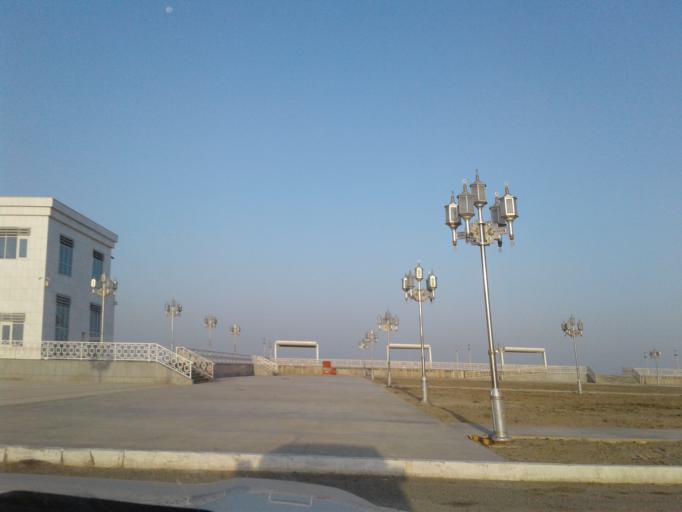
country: IR
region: Golestan
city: Aq Qayeh
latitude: 37.7057
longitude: 54.7419
